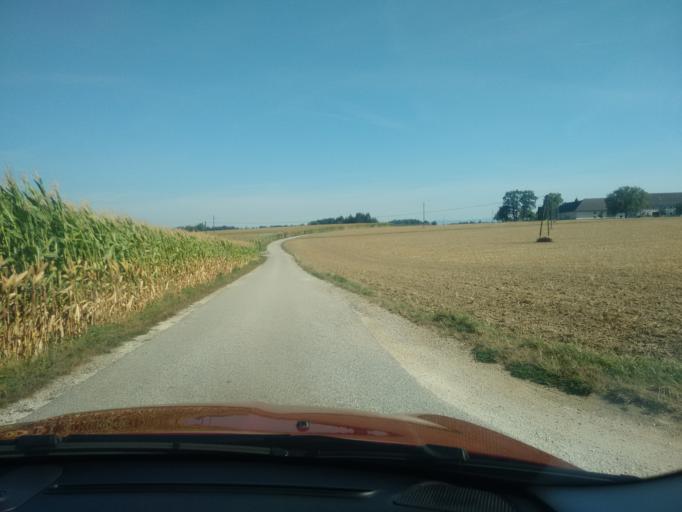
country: AT
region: Upper Austria
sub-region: Wels-Land
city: Sattledt
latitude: 48.0882
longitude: 14.0762
